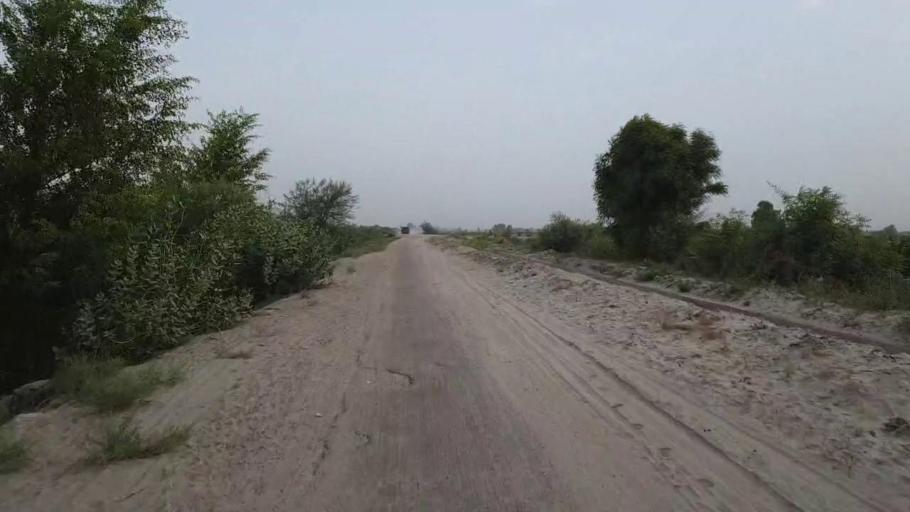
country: PK
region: Sindh
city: Daur
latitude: 26.4159
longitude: 68.2251
